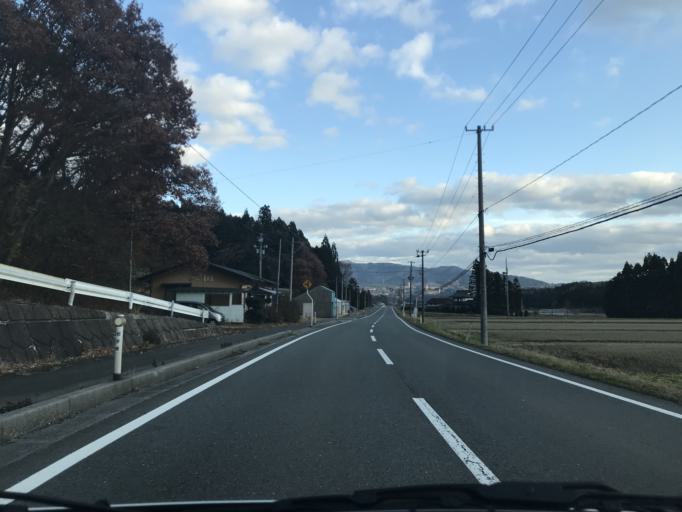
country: JP
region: Iwate
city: Mizusawa
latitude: 39.0465
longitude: 141.0997
